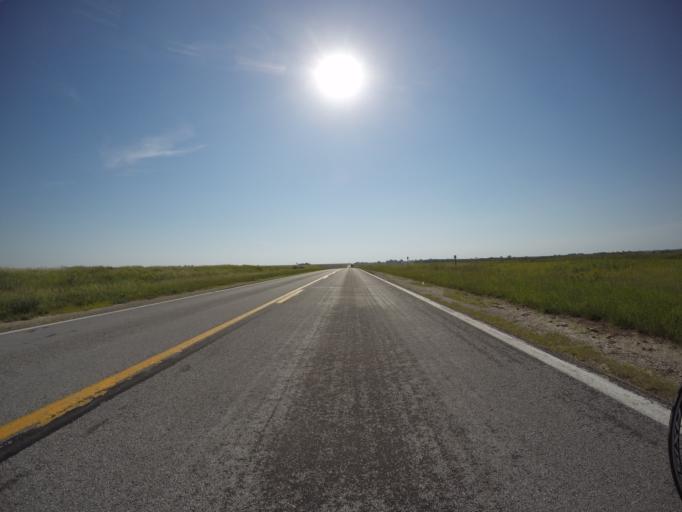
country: US
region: Nebraska
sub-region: Pawnee County
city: Pawnee City
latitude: 40.0446
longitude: -96.3830
